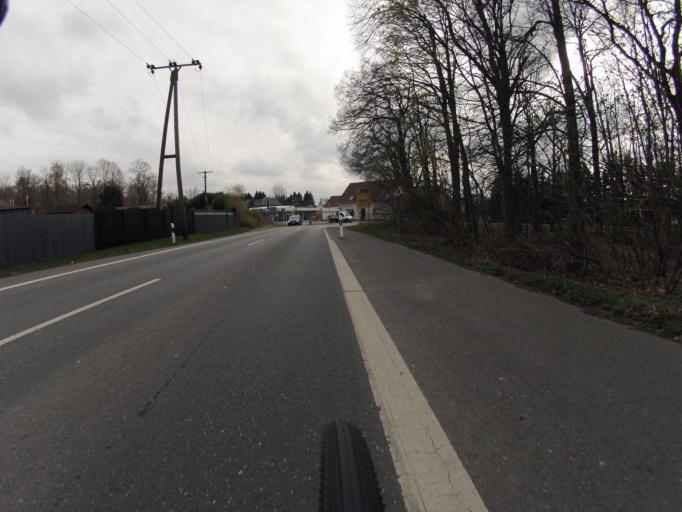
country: DE
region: North Rhine-Westphalia
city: Ibbenburen
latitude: 52.3016
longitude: 7.6914
